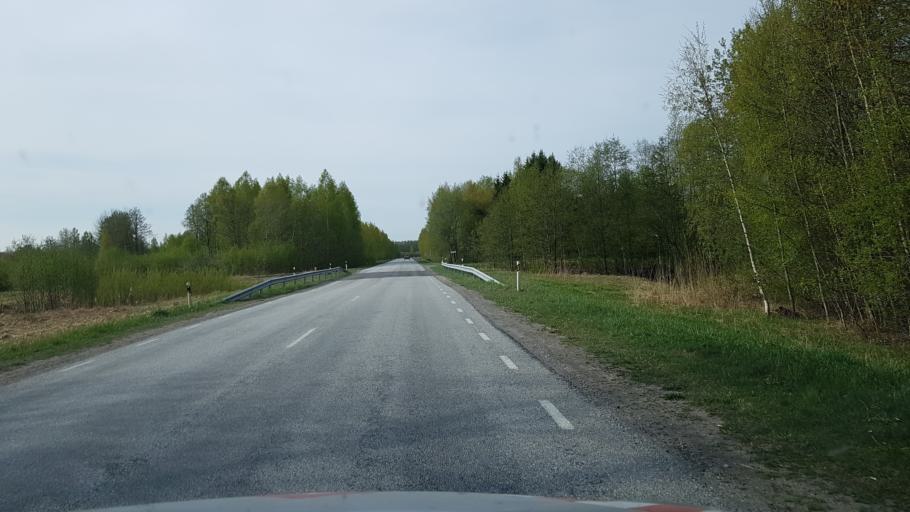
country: EE
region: Paernumaa
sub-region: Audru vald
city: Audru
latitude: 58.4113
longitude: 24.3089
